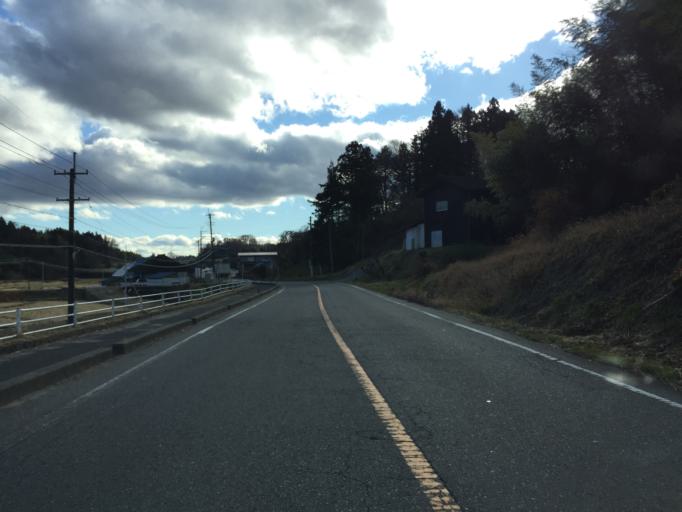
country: JP
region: Fukushima
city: Nihommatsu
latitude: 37.5922
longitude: 140.5778
